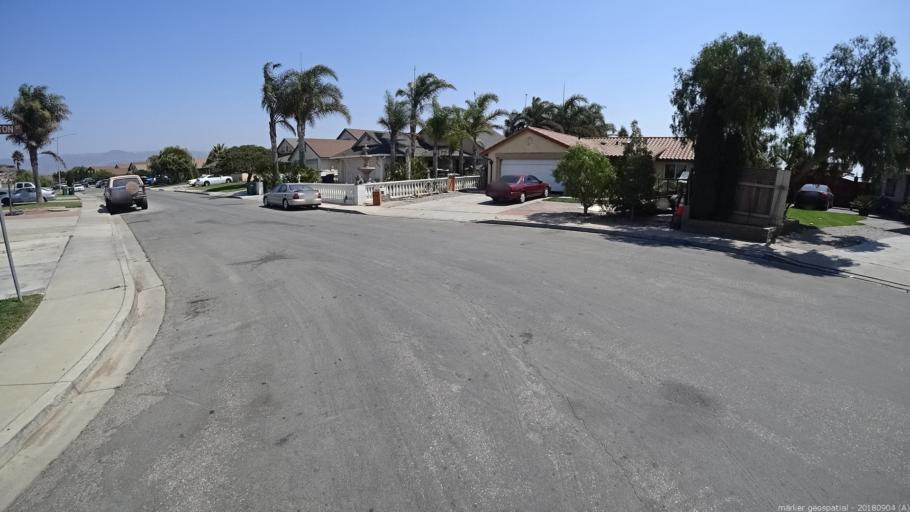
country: US
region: California
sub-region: Monterey County
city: Chualar
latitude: 36.5669
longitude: -121.5127
